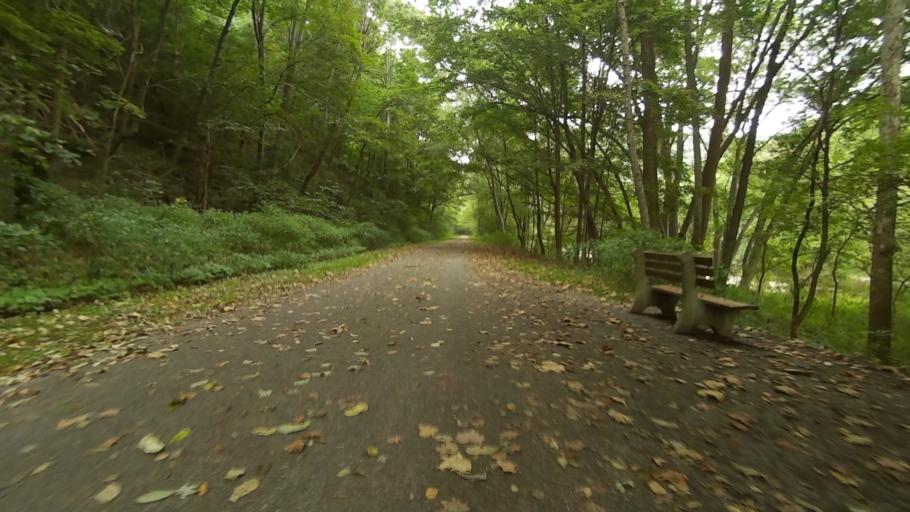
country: US
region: Pennsylvania
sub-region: Blair County
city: Williamsburg
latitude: 40.5663
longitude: -78.1376
